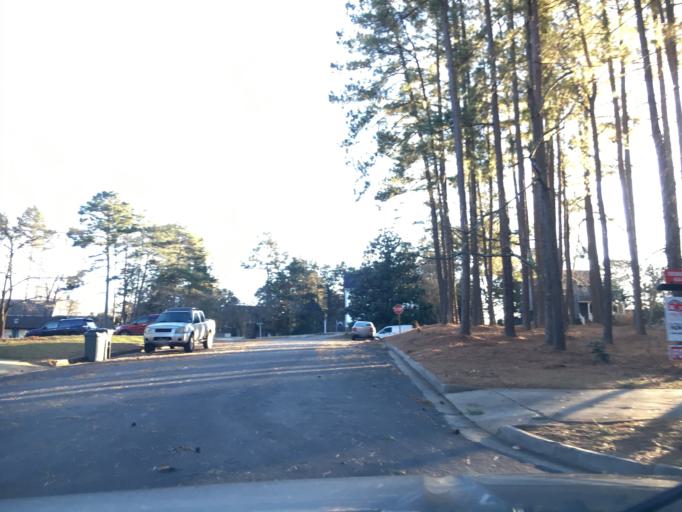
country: US
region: Virginia
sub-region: Halifax County
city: South Boston
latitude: 36.7076
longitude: -78.8837
